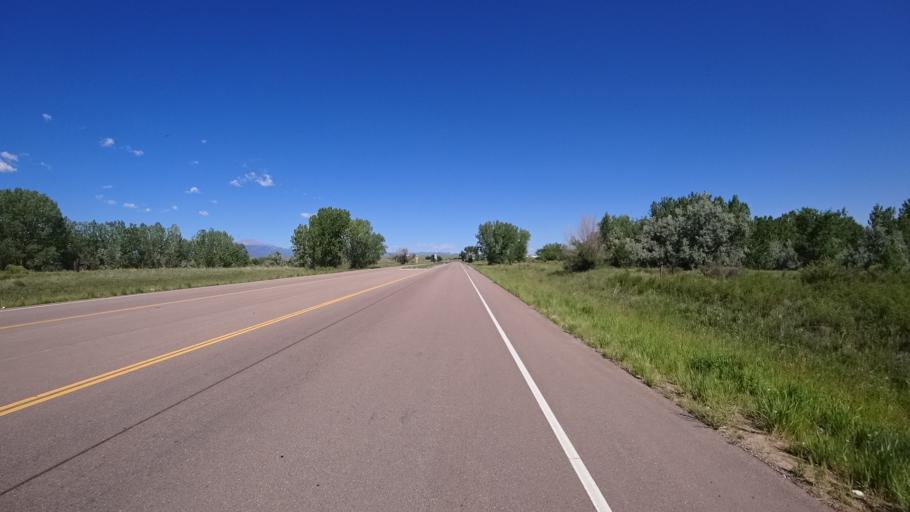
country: US
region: Colorado
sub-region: El Paso County
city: Security-Widefield
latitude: 38.7514
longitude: -104.6534
